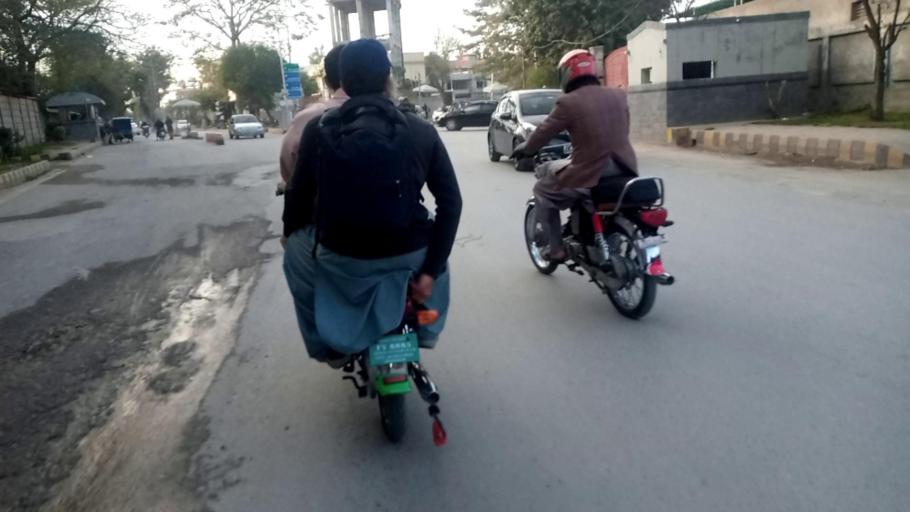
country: PK
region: Khyber Pakhtunkhwa
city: Peshawar
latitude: 34.0192
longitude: 71.5542
